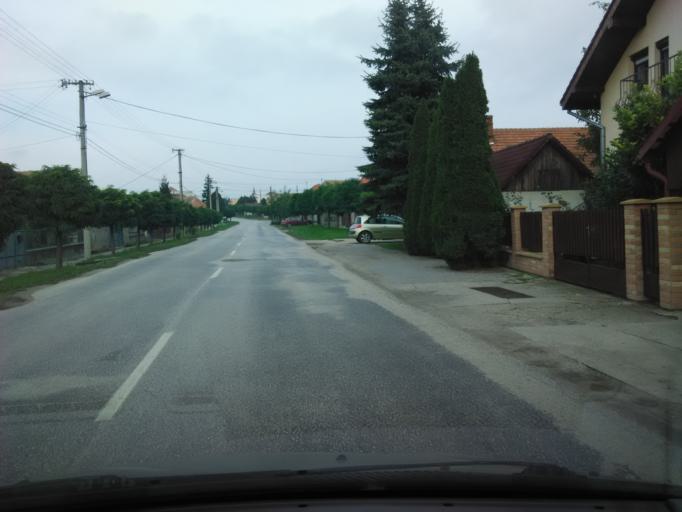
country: SK
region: Nitriansky
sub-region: Okres Nove Zamky
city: Nove Zamky
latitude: 47.9867
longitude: 18.2660
